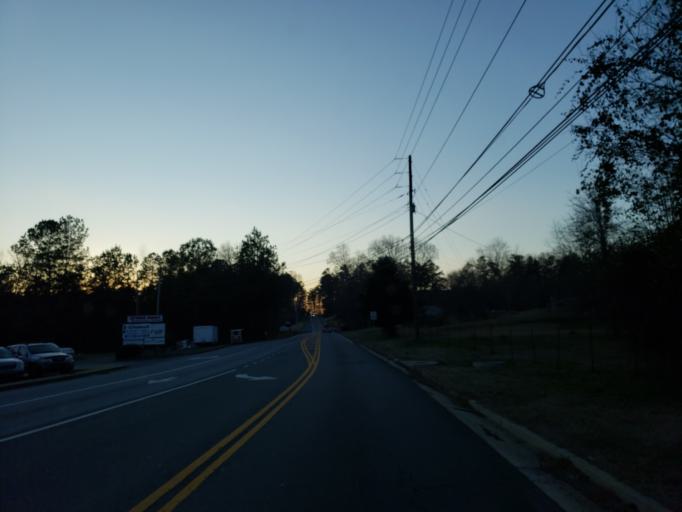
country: US
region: Georgia
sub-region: Cherokee County
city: Woodstock
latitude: 34.1183
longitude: -84.4699
